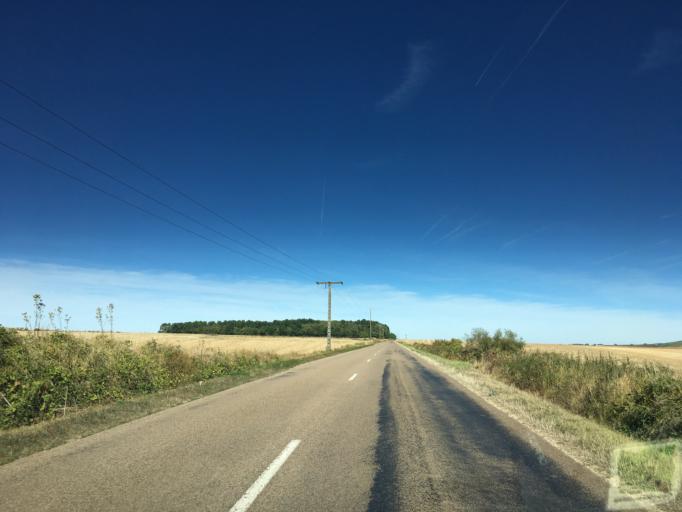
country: FR
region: Bourgogne
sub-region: Departement de l'Yonne
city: Vermenton
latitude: 47.6691
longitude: 3.6602
